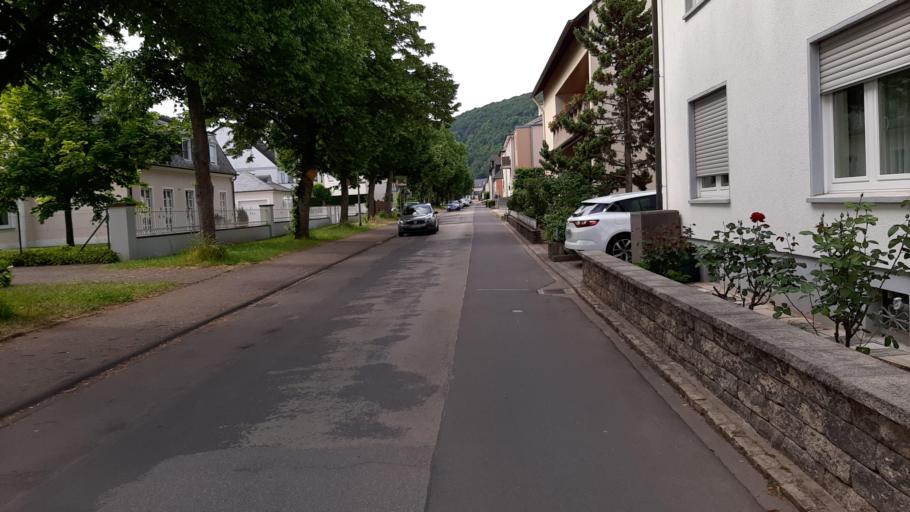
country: DE
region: Rheinland-Pfalz
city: Konz
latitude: 49.7161
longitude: 6.5844
